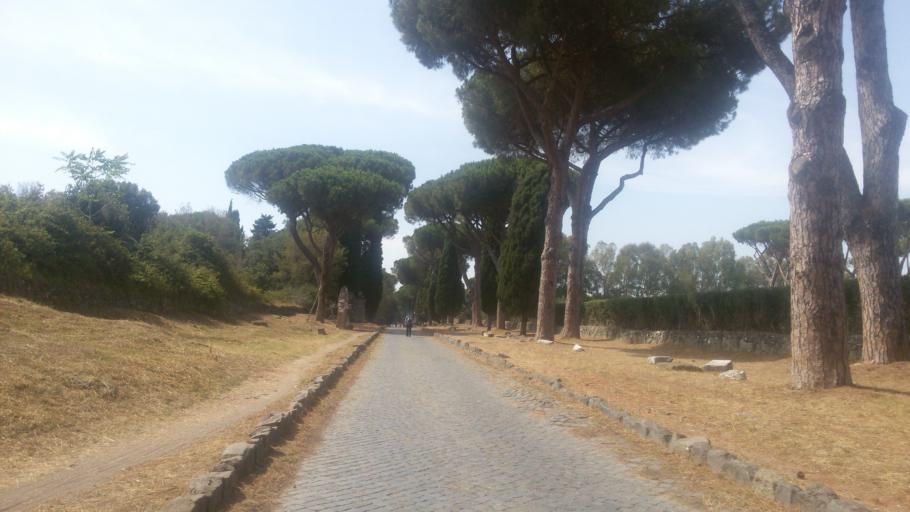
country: IT
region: Latium
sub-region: Citta metropolitana di Roma Capitale
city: Rome
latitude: 41.8376
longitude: 12.5369
